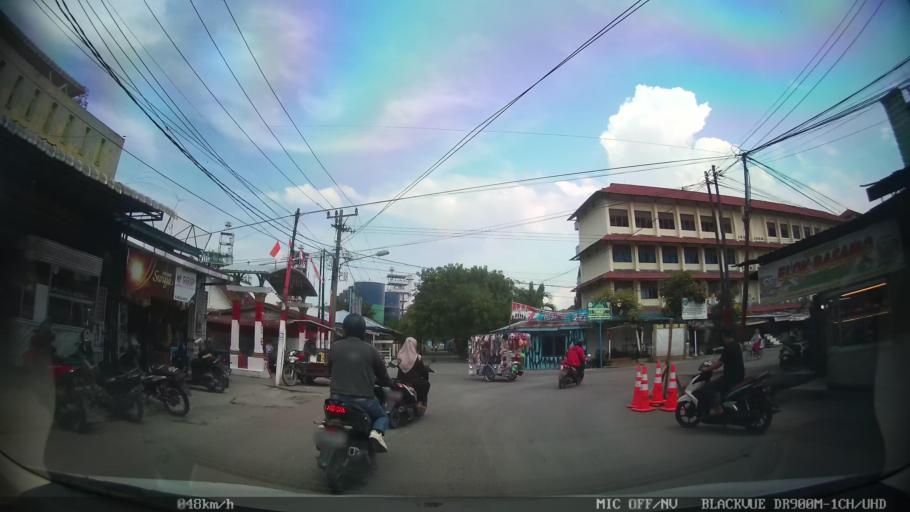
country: ID
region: North Sumatra
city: Labuhan Deli
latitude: 3.6686
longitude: 98.6803
